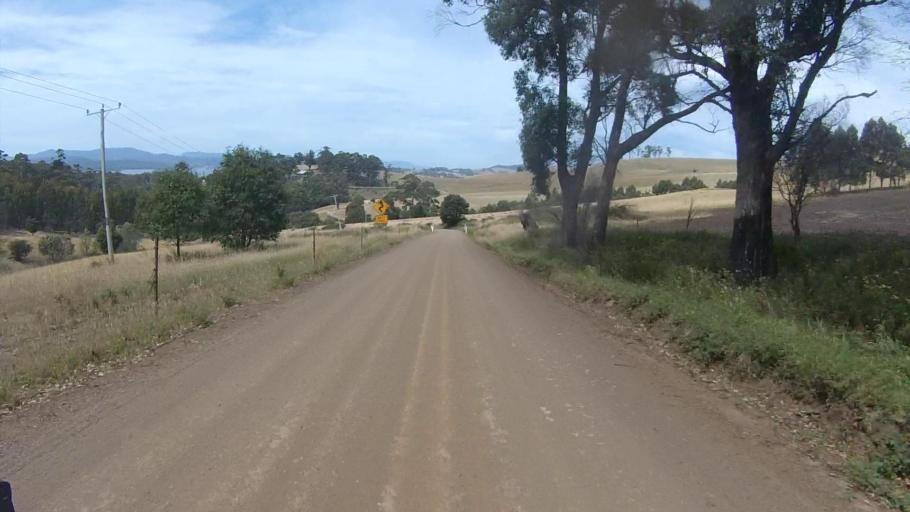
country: AU
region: Tasmania
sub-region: Sorell
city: Sorell
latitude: -42.7837
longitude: 147.8429
